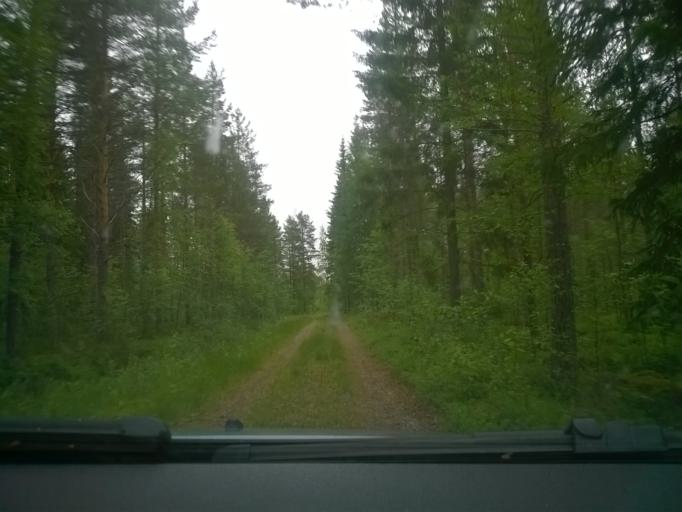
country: FI
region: Kainuu
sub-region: Kehys-Kainuu
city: Kuhmo
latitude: 64.4510
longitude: 29.7229
